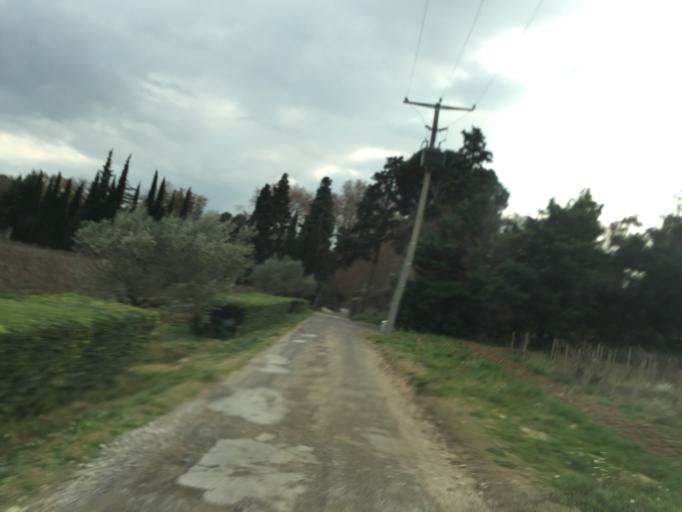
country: FR
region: Provence-Alpes-Cote d'Azur
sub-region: Departement du Vaucluse
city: Chateauneuf-du-Pape
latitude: 44.0503
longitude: 4.8582
